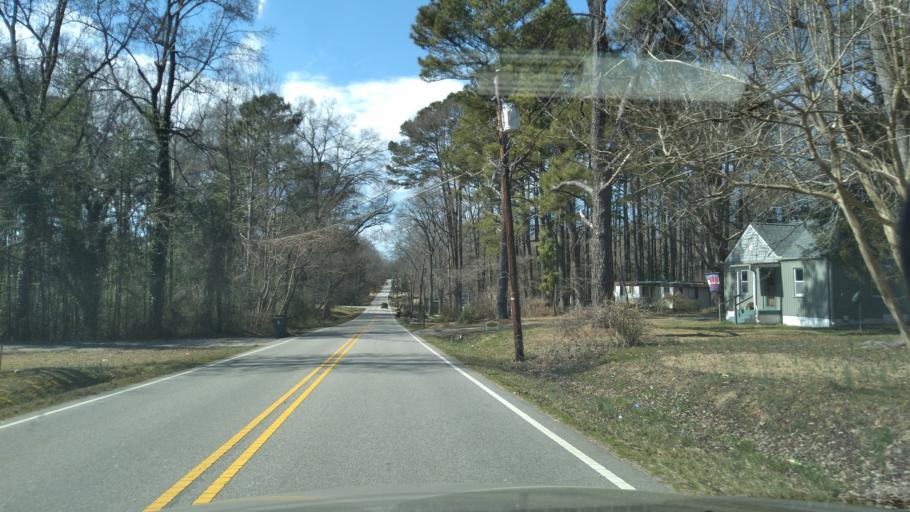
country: US
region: North Carolina
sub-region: Wake County
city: Garner
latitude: 35.7097
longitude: -78.6468
